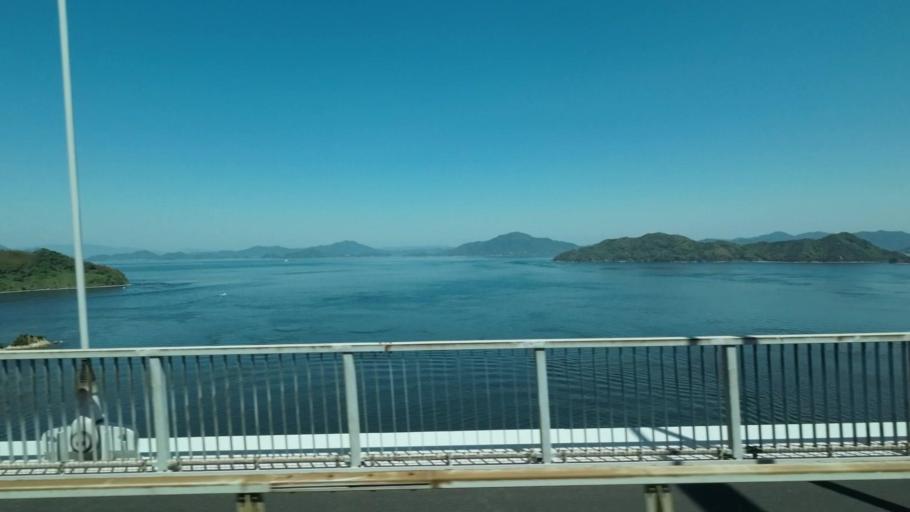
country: JP
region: Hiroshima
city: Takehara
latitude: 34.1199
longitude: 132.9989
